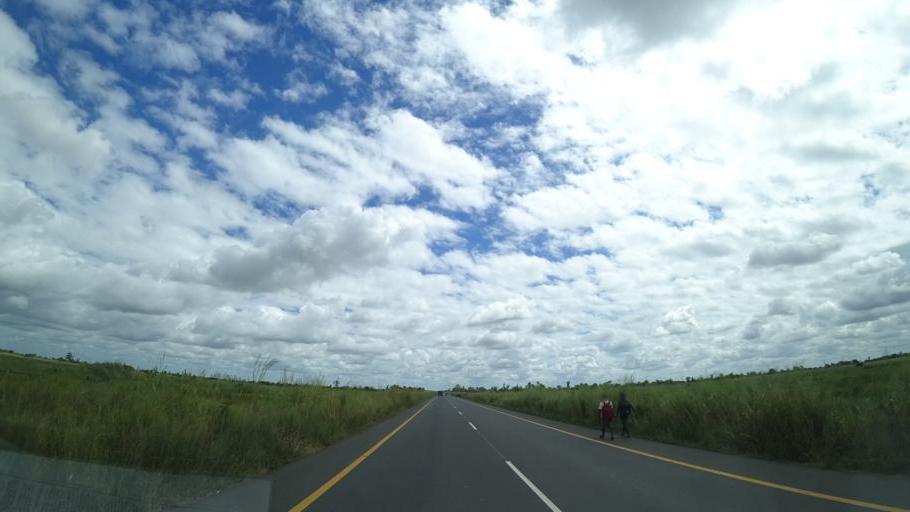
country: MZ
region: Sofala
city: Dondo
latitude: -19.3874
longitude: 34.4134
